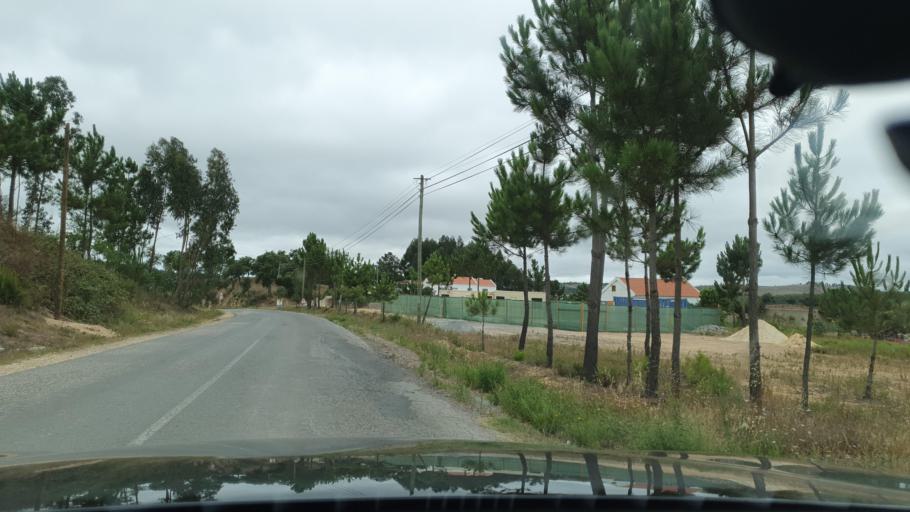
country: PT
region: Beja
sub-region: Odemira
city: Sao Teotonio
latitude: 37.5046
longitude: -8.6914
